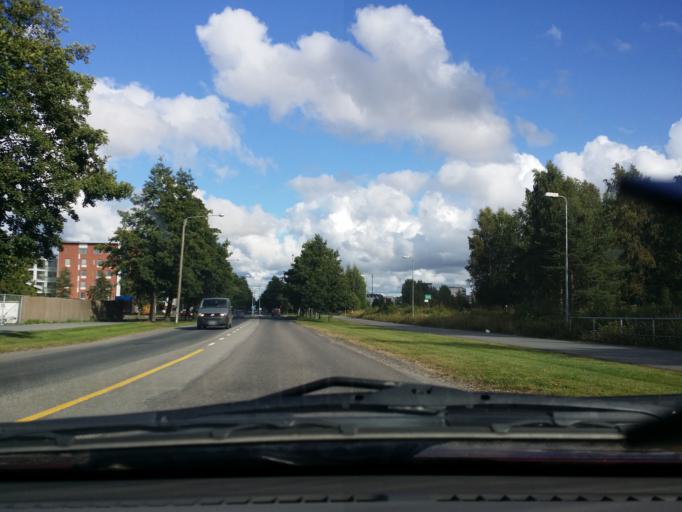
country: FI
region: Satakunta
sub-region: Pori
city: Pori
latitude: 61.4886
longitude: 21.7696
